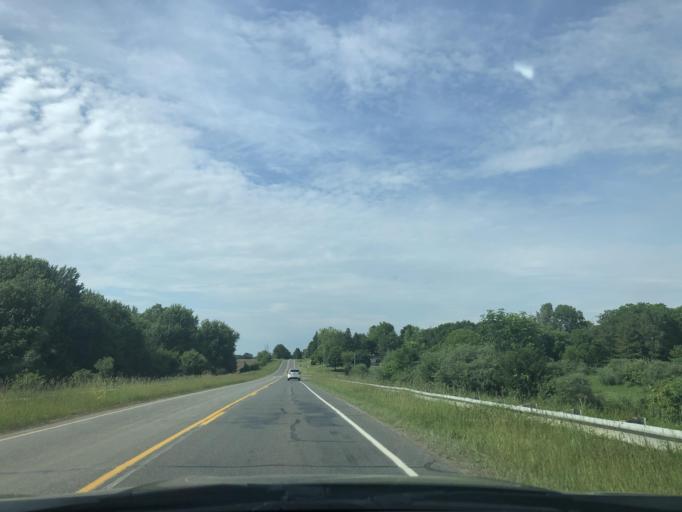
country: US
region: Michigan
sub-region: Clinton County
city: Bath
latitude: 42.8044
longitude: -84.4837
